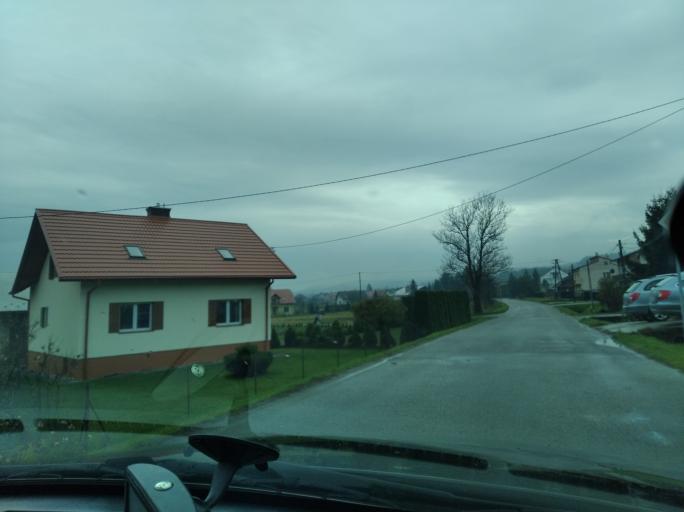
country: PL
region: Subcarpathian Voivodeship
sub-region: Powiat strzyzowski
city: Czudec
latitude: 49.9338
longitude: 21.8462
